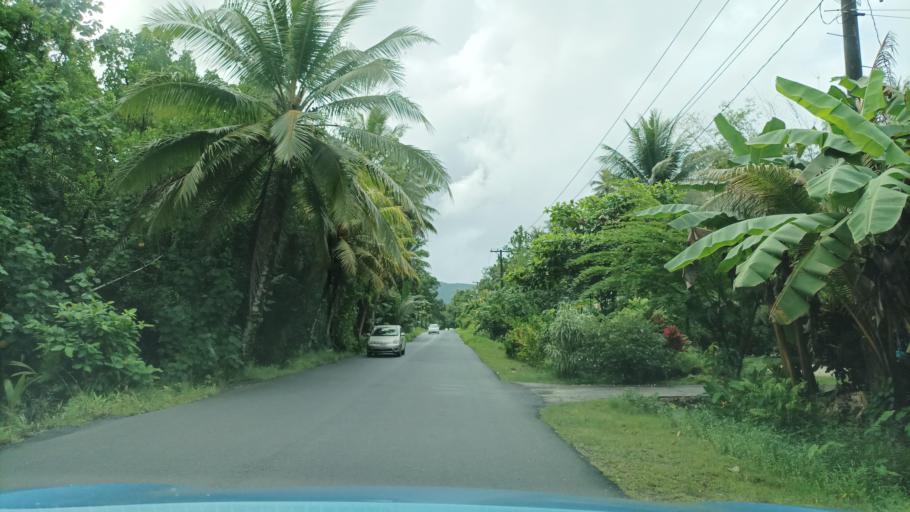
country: FM
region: Pohnpei
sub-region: Kolonia Municipality
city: Kolonia
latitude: 6.9397
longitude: 158.2778
